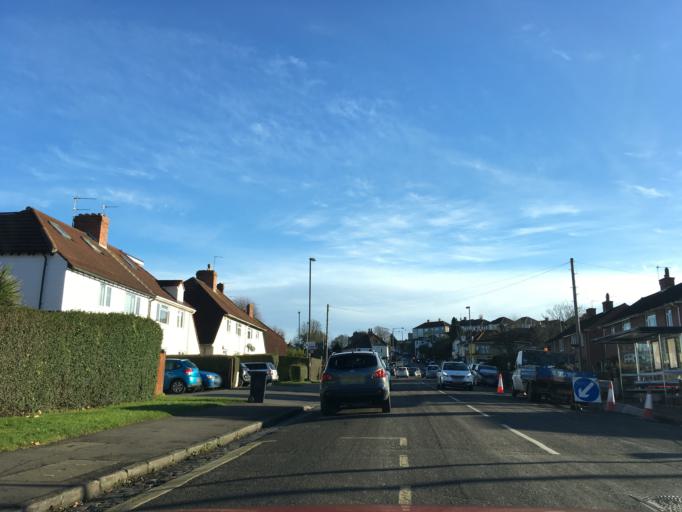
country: GB
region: England
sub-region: South Gloucestershire
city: Kingswood
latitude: 51.4711
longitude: -2.5216
